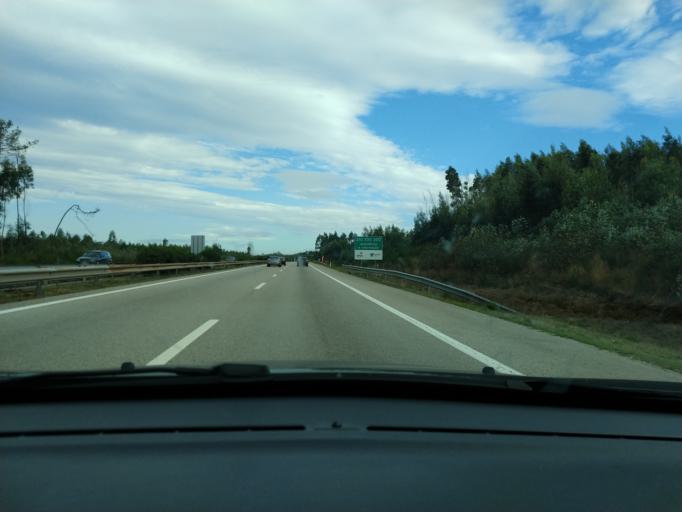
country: PT
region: Aveiro
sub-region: Albergaria-A-Velha
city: Albergaria-a-Velha
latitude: 40.7025
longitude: -8.5226
